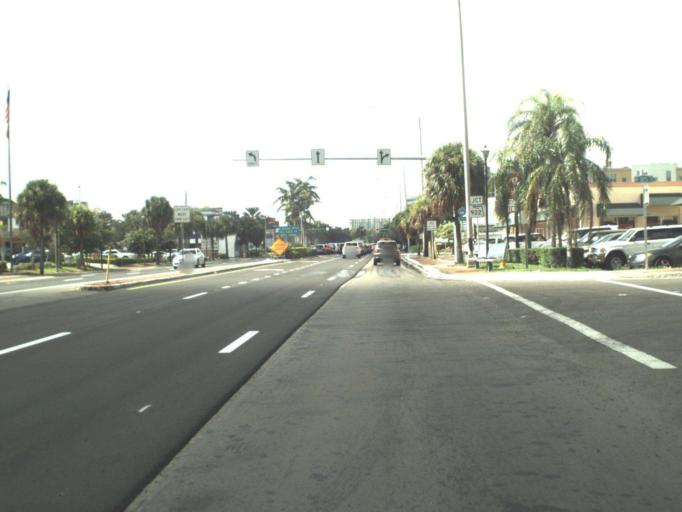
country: US
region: Florida
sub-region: Miami-Dade County
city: Biscayne Park
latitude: 25.8918
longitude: -80.1631
